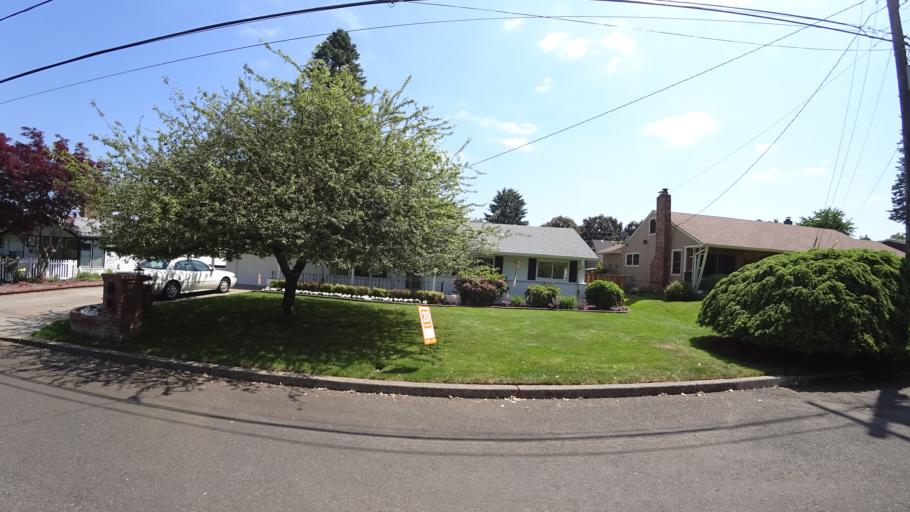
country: US
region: Oregon
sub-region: Multnomah County
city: Fairview
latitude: 45.5291
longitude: -122.5072
